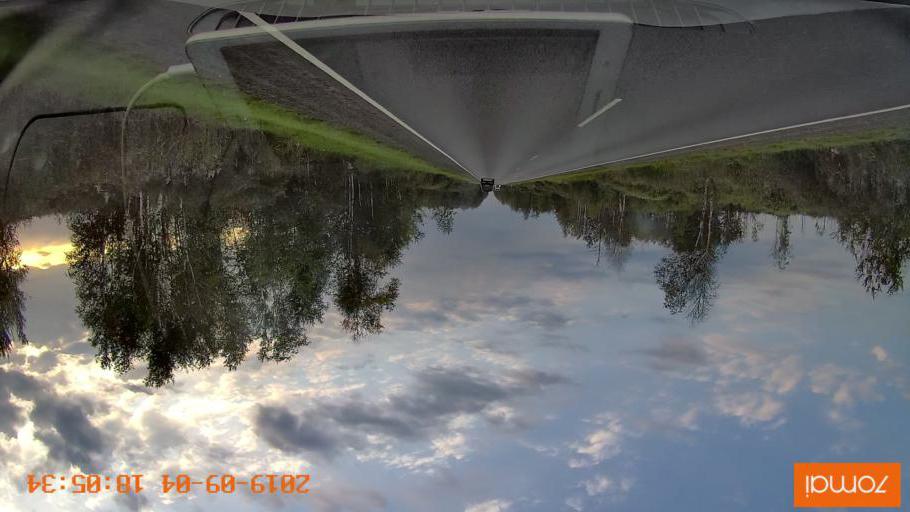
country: RU
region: Moskovskaya
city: Il'inskiy Pogost
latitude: 55.4399
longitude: 38.8249
